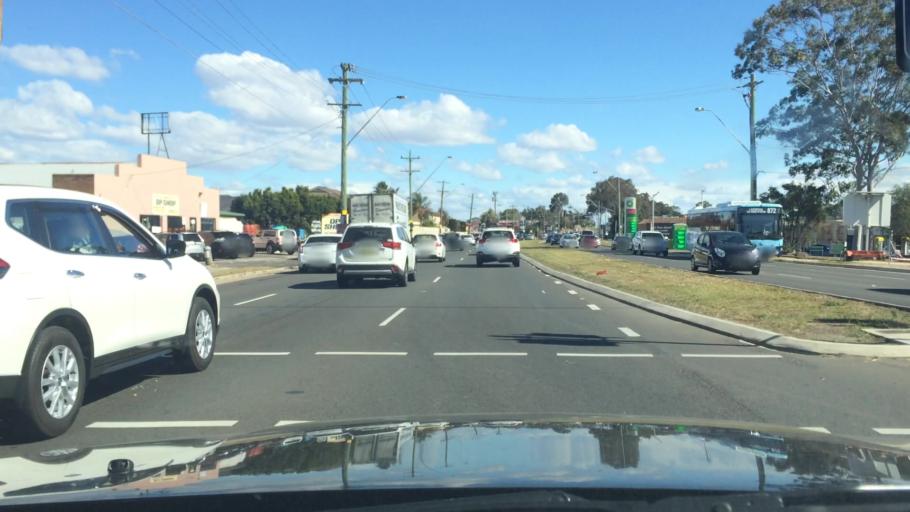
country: AU
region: New South Wales
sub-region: Campbelltown Municipality
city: Glenfield
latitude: -33.9551
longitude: 150.8962
